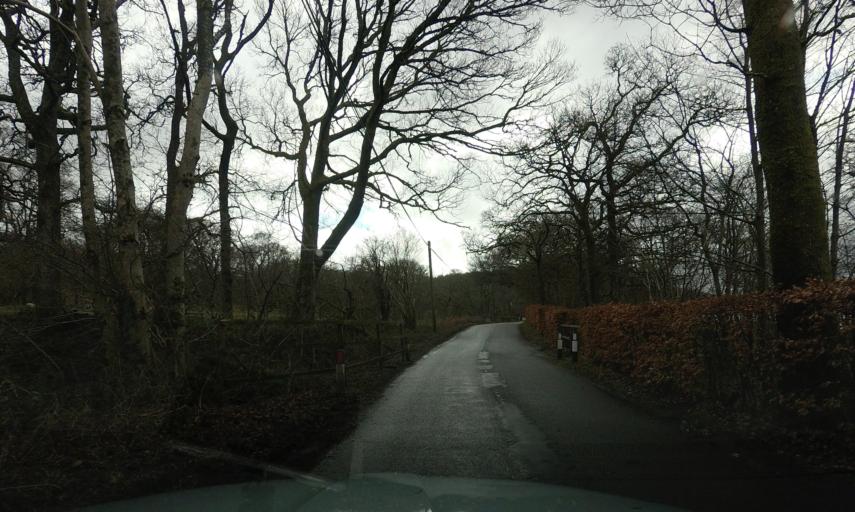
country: GB
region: Scotland
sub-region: West Dunbartonshire
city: Balloch
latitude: 56.0982
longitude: -4.5561
